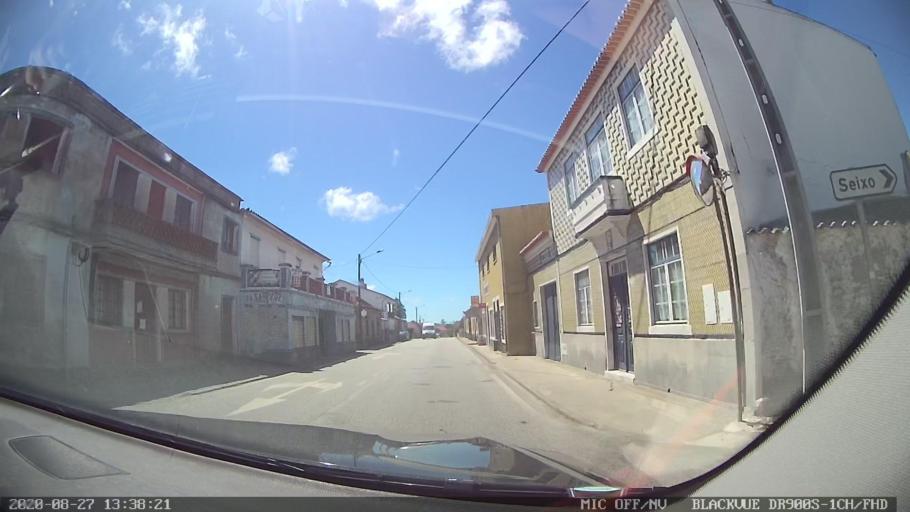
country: PT
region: Coimbra
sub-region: Mira
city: Mira
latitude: 40.4468
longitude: -8.7233
